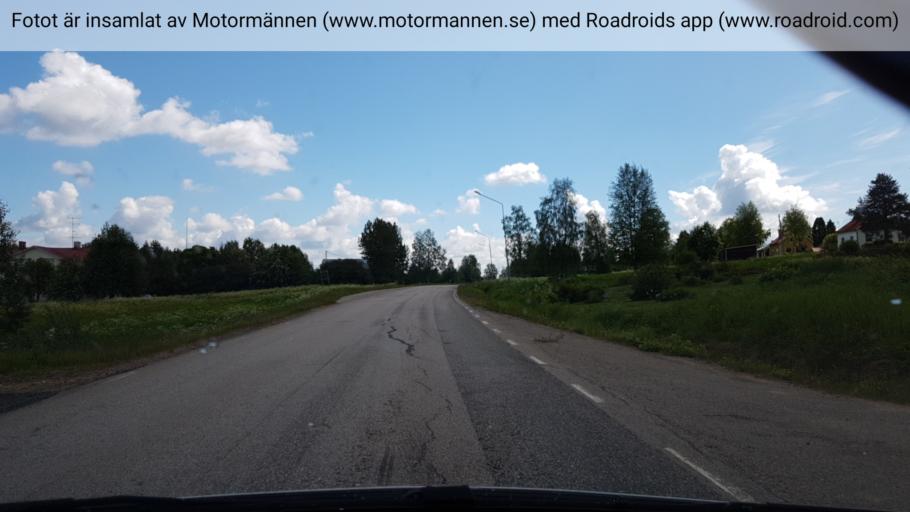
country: FI
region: Lapland
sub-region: Torniolaakso
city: Ylitornio
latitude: 66.1749
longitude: 23.8047
